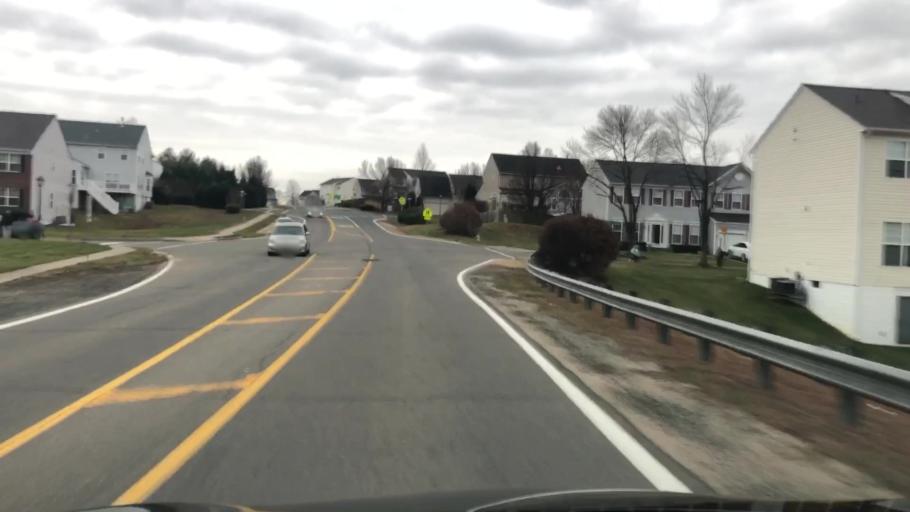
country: US
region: Virginia
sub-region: Stafford County
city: Falmouth
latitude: 38.3678
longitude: -77.5008
